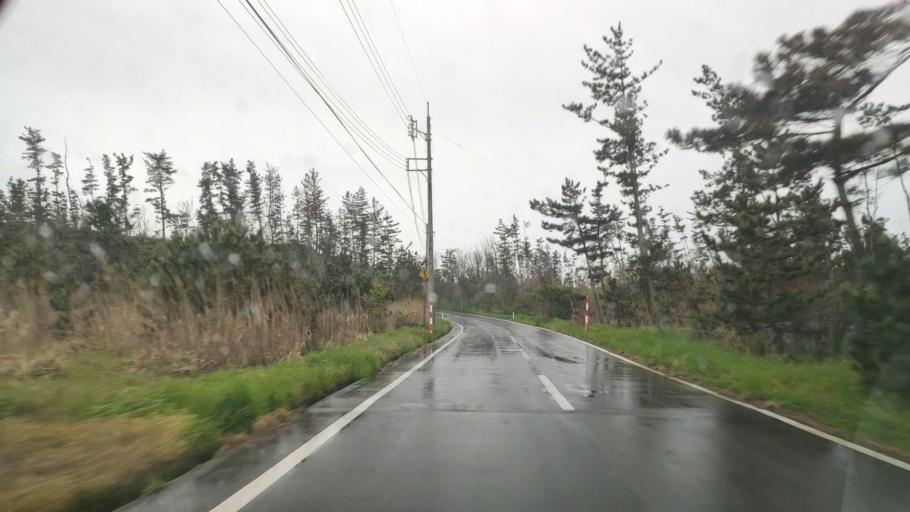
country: JP
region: Akita
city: Noshiromachi
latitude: 40.0809
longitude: 139.9547
